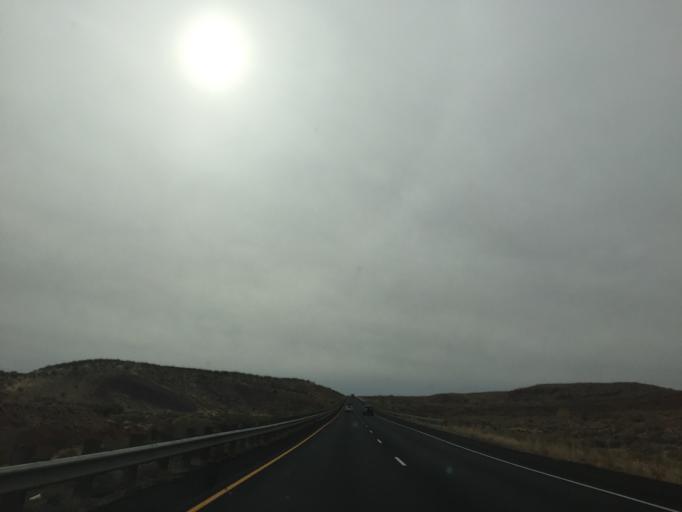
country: US
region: Utah
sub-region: Washington County
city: Hurricane
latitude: 37.1952
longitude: -113.4052
